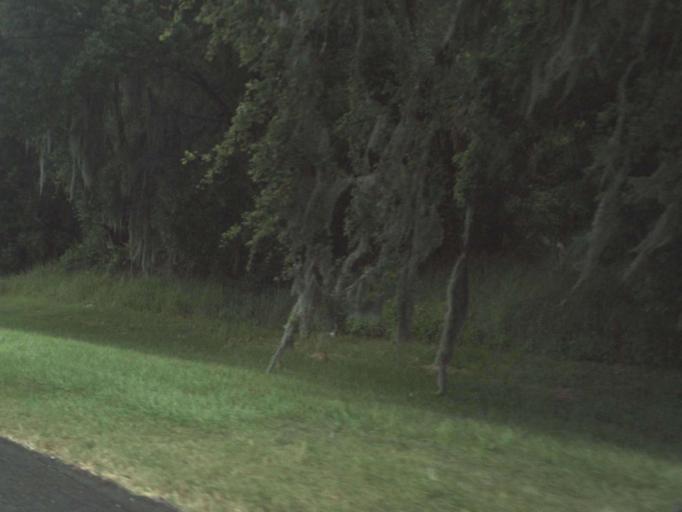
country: US
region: Florida
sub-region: Marion County
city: Citra
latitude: 29.3252
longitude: -82.1518
